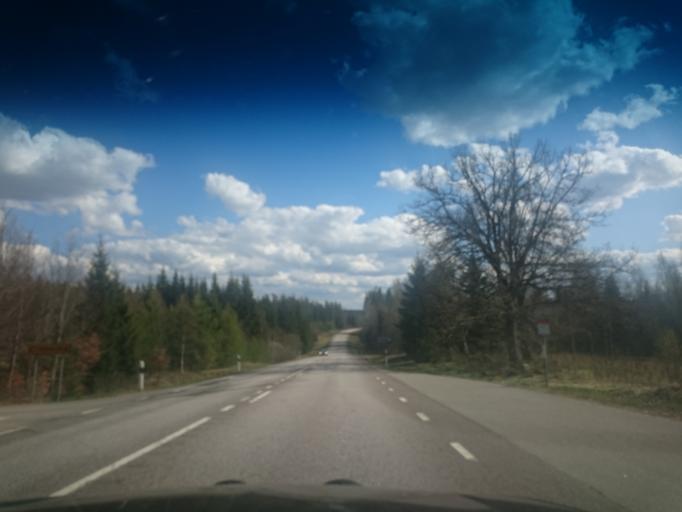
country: SE
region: Joenkoeping
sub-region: Vetlanda Kommun
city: Vetlanda
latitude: 57.2441
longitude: 15.1403
